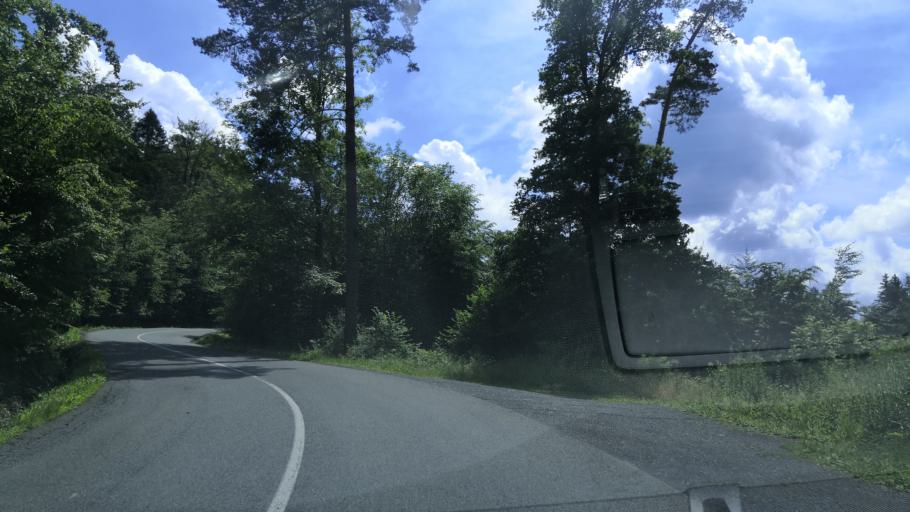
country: CZ
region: Zlin
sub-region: Okres Vsetin
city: Roznov pod Radhostem
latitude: 49.4355
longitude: 18.1316
